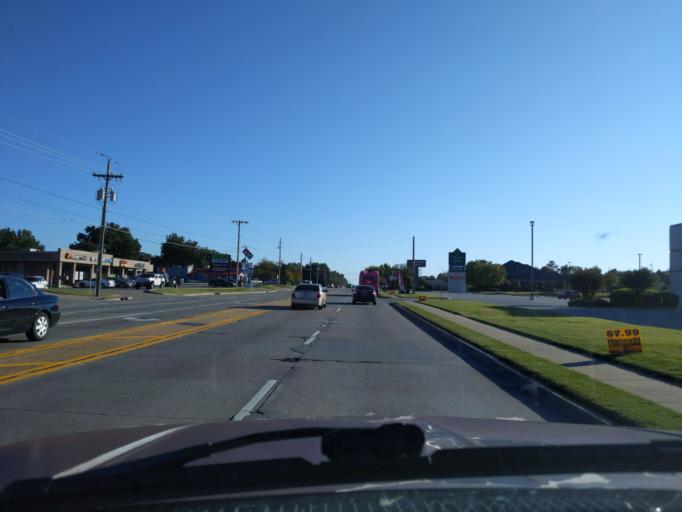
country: US
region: Oklahoma
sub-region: Tulsa County
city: Broken Arrow
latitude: 36.1188
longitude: -95.8512
